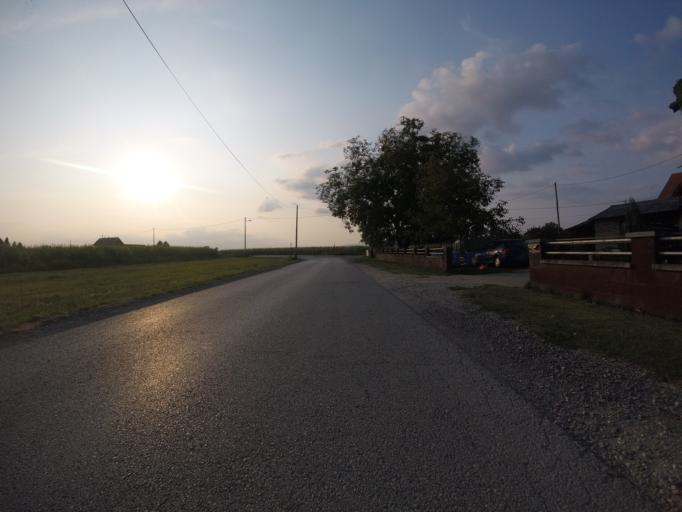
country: HR
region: Zagrebacka
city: Micevec
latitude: 45.7527
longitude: 16.1284
